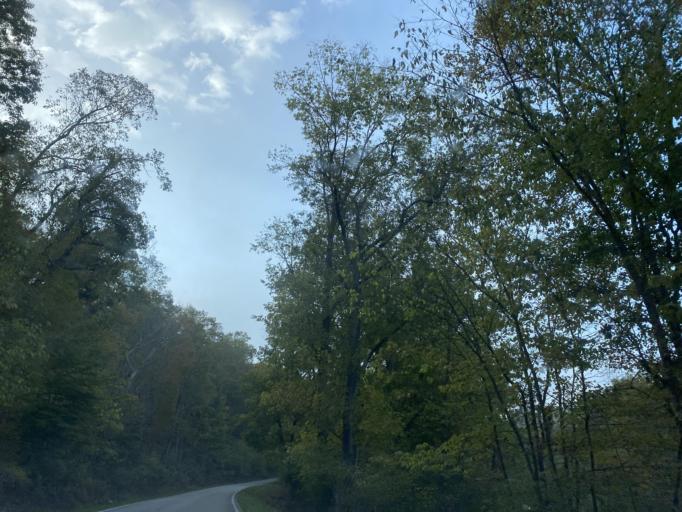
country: US
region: Kentucky
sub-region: Pendleton County
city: Falmouth
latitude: 38.7446
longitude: -84.3167
